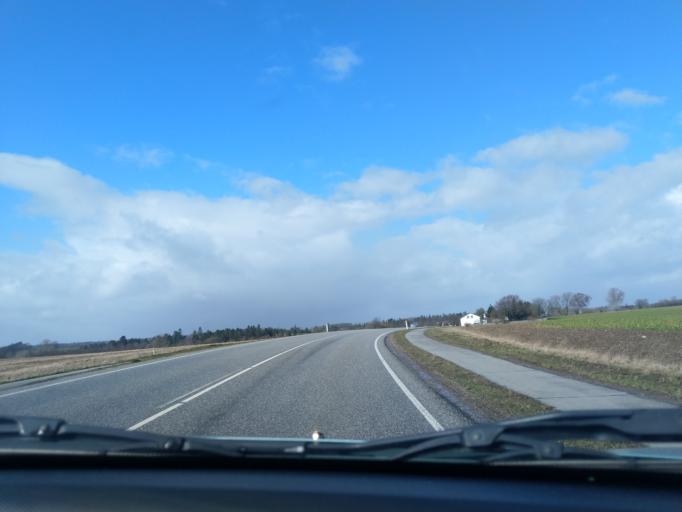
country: DK
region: Zealand
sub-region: Naestved Kommune
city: Naestved
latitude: 55.2952
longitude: 11.6954
